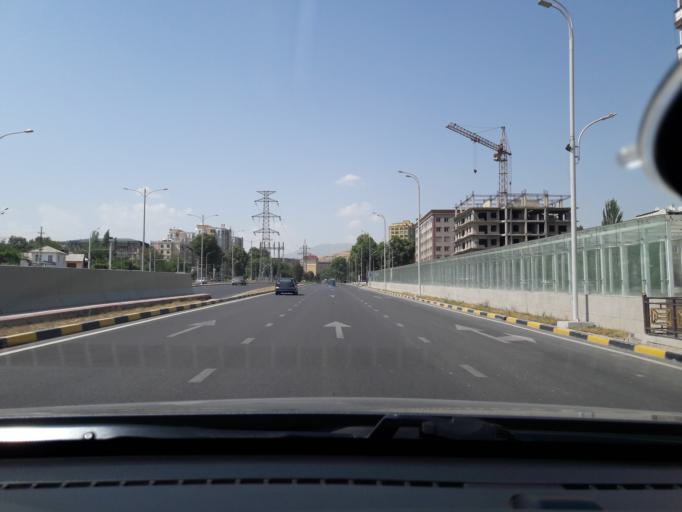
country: TJ
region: Dushanbe
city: Dushanbe
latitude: 38.5848
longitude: 68.7413
